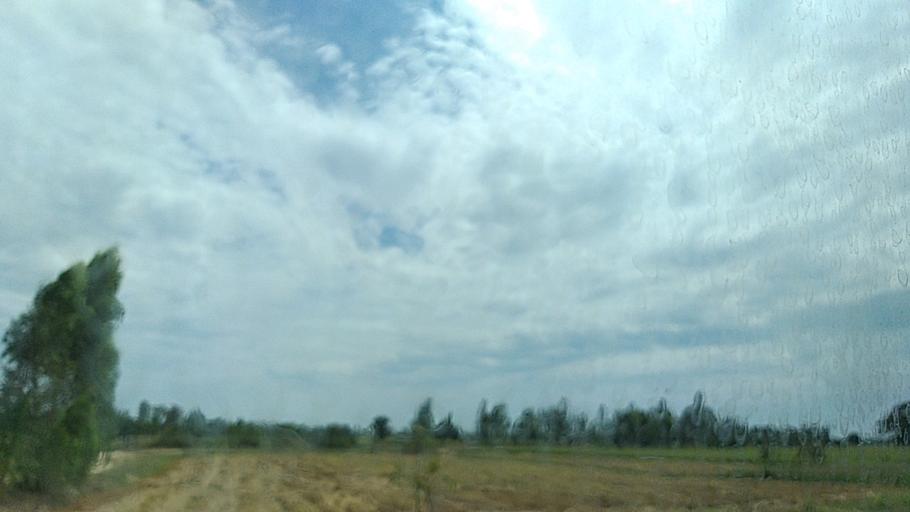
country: TH
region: Maha Sarakham
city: Chiang Yuen
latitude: 16.3816
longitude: 103.1034
